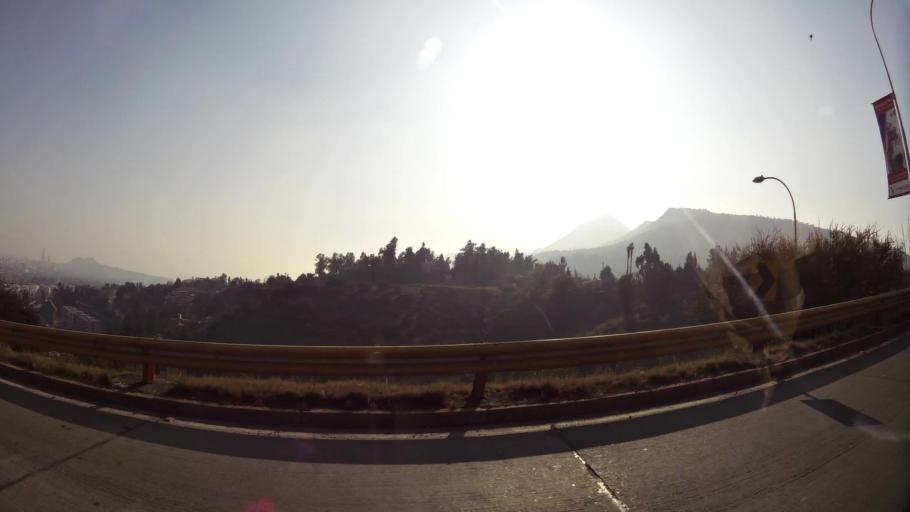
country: CL
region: Santiago Metropolitan
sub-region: Provincia de Santiago
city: Villa Presidente Frei, Nunoa, Santiago, Chile
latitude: -33.3688
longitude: -70.5446
